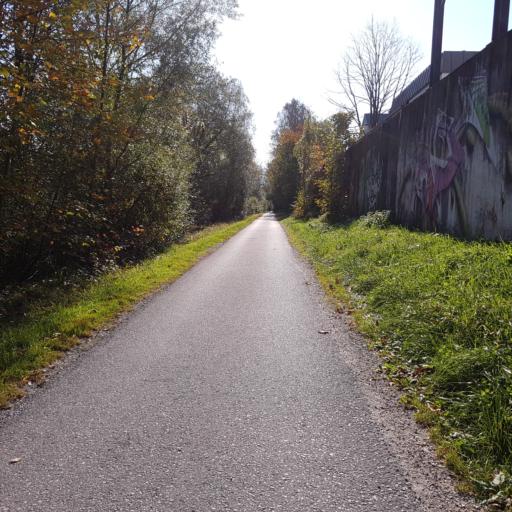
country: AT
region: Salzburg
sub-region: Politischer Bezirk Hallein
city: Oberalm
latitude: 47.6978
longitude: 13.0793
